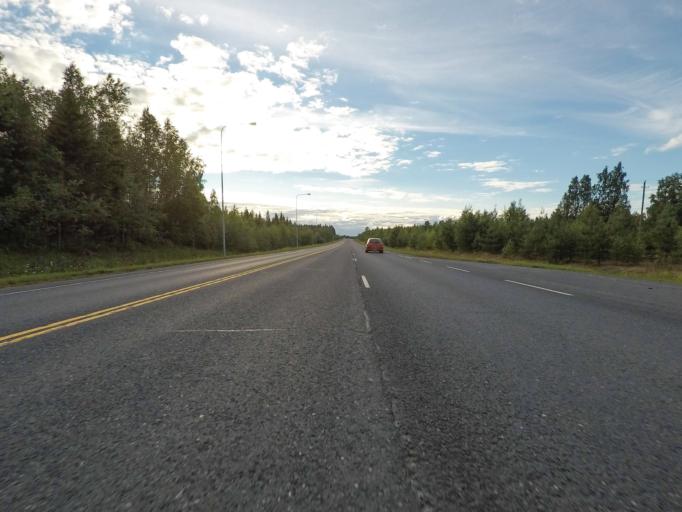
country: FI
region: Northern Savo
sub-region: Kuopio
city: Kuopio
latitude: 62.9766
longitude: 27.8047
